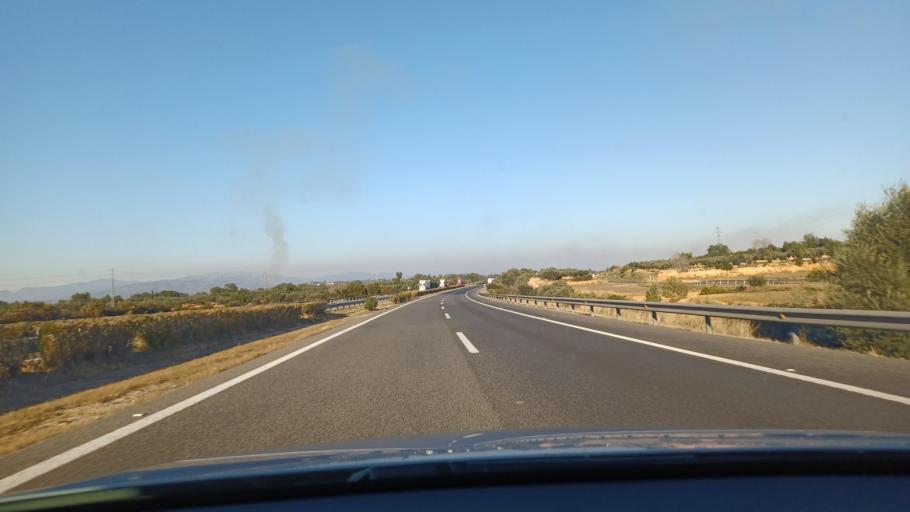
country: ES
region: Catalonia
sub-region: Provincia de Tarragona
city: Masdenverge
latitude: 40.6898
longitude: 0.5290
